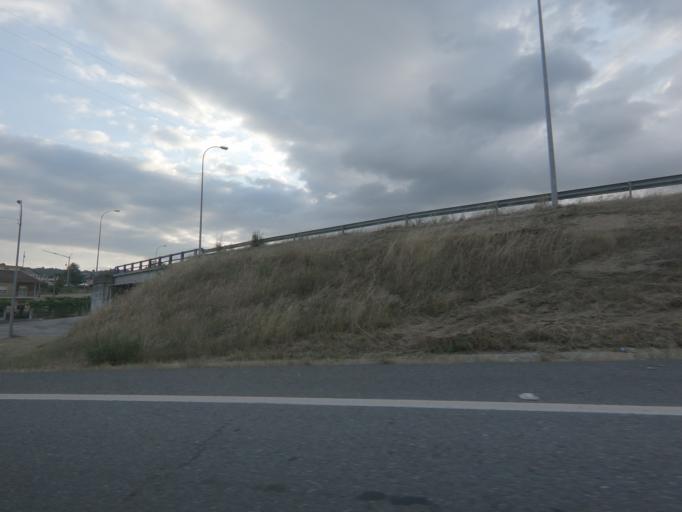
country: ES
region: Galicia
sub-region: Provincia de Ourense
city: Taboadela
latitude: 42.2839
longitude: -7.8402
